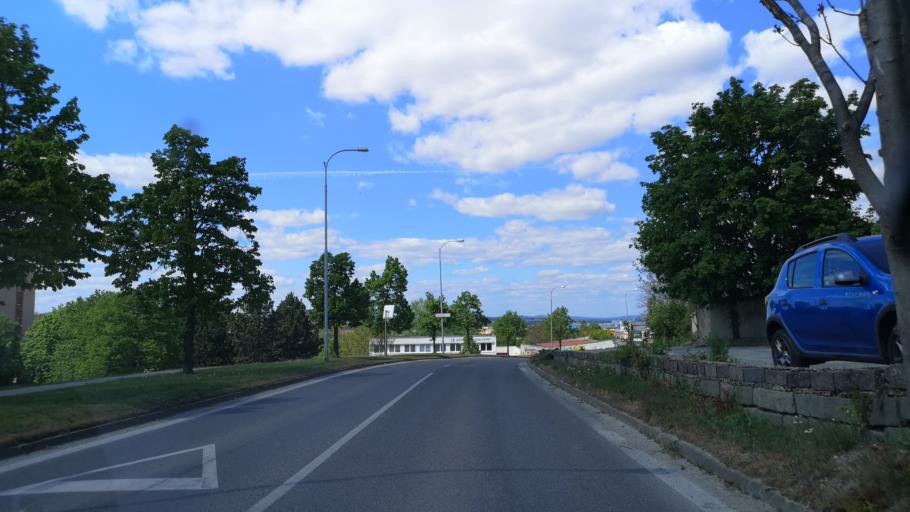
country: SK
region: Nitriansky
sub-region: Okres Nitra
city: Nitra
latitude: 48.3066
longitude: 18.0681
